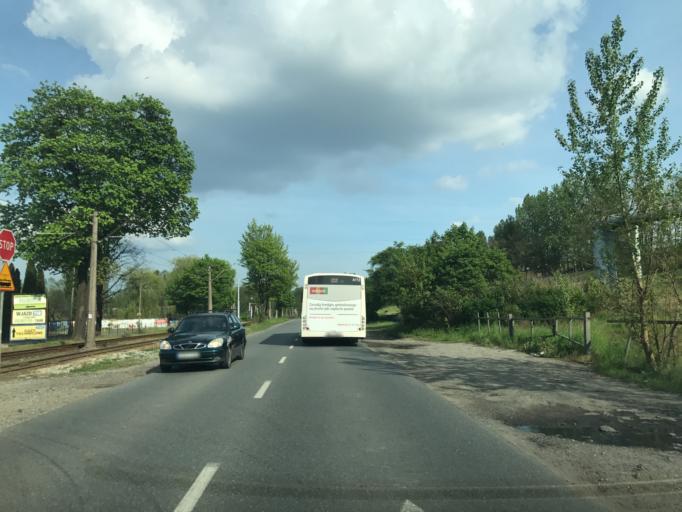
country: PL
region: Kujawsko-Pomorskie
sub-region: Powiat bydgoski
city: Osielsko
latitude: 53.1170
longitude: 18.0938
